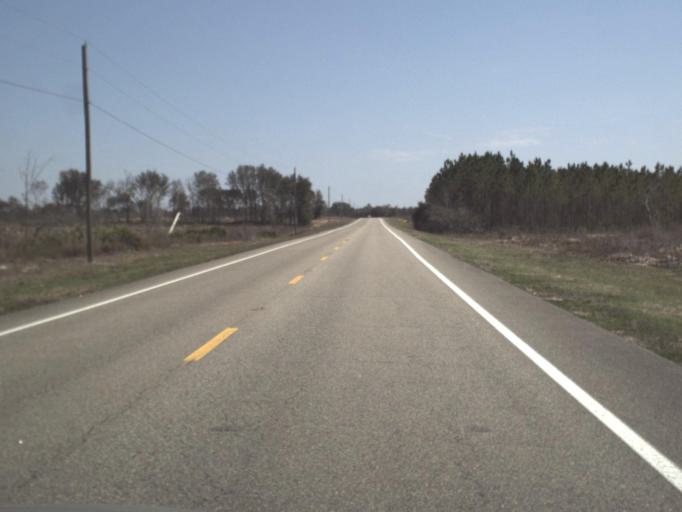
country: US
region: Florida
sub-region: Liberty County
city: Bristol
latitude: 30.5054
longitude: -84.8595
